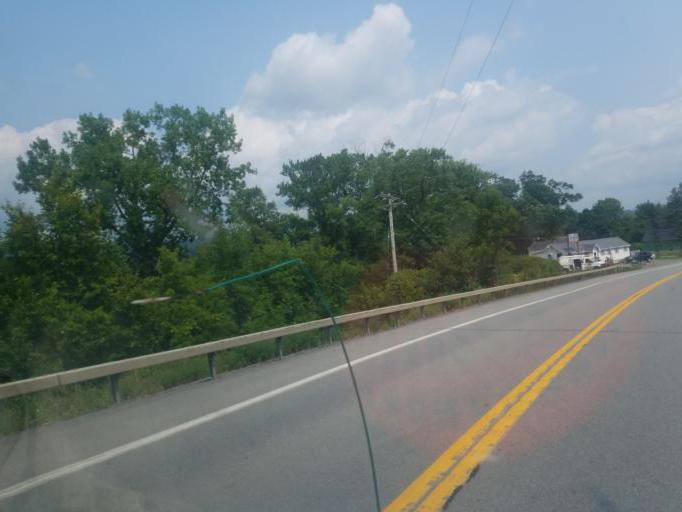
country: US
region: New York
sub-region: Herkimer County
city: Herkimer
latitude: 43.0140
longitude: -74.9241
